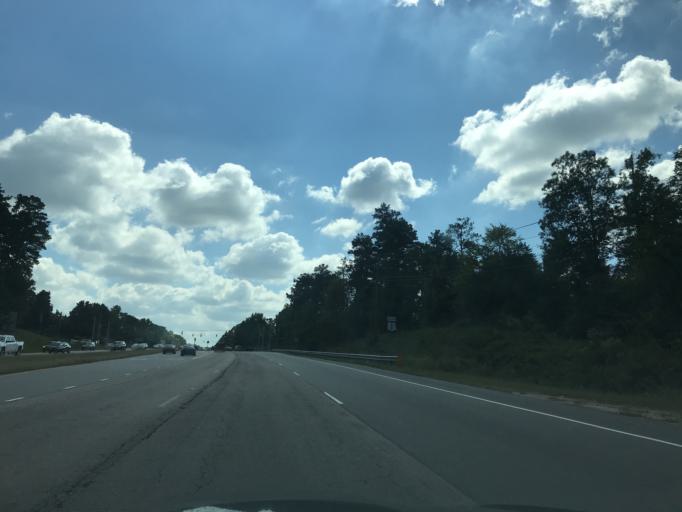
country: US
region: North Carolina
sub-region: Wake County
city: Wake Forest
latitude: 35.9595
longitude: -78.5423
